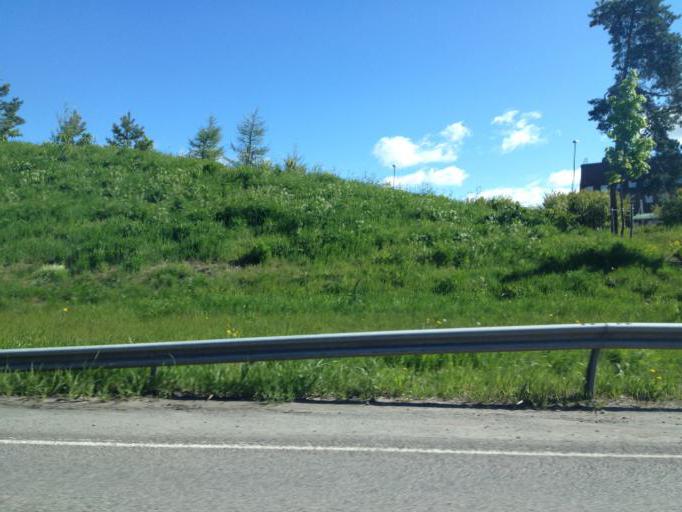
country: FI
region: Uusimaa
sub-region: Helsinki
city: Vantaa
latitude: 60.2264
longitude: 25.0773
